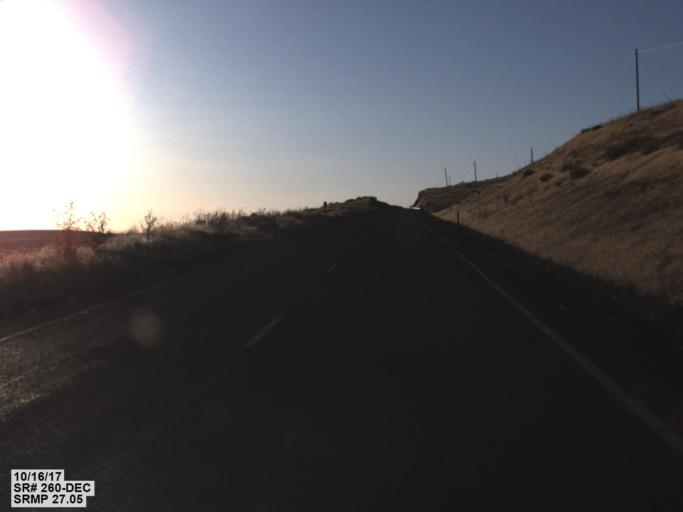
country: US
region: Washington
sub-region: Franklin County
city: Connell
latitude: 46.6504
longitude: -118.5112
